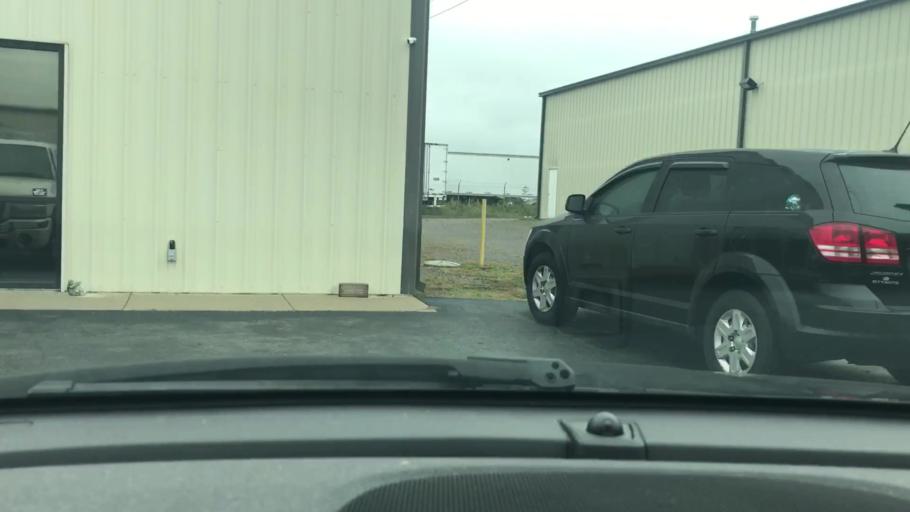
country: US
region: Tennessee
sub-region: Rutherford County
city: La Vergne
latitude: 36.0251
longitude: -86.5601
